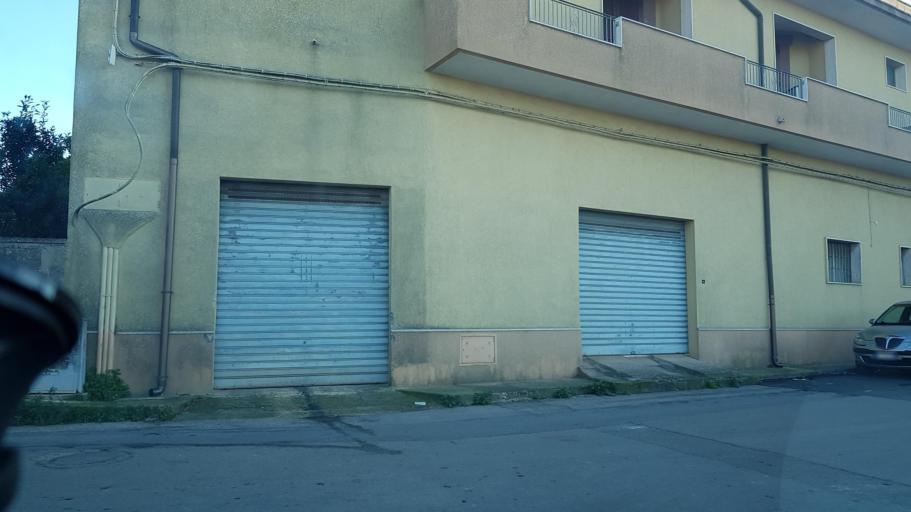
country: IT
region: Apulia
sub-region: Provincia di Brindisi
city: Latiano
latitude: 40.5548
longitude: 17.7243
